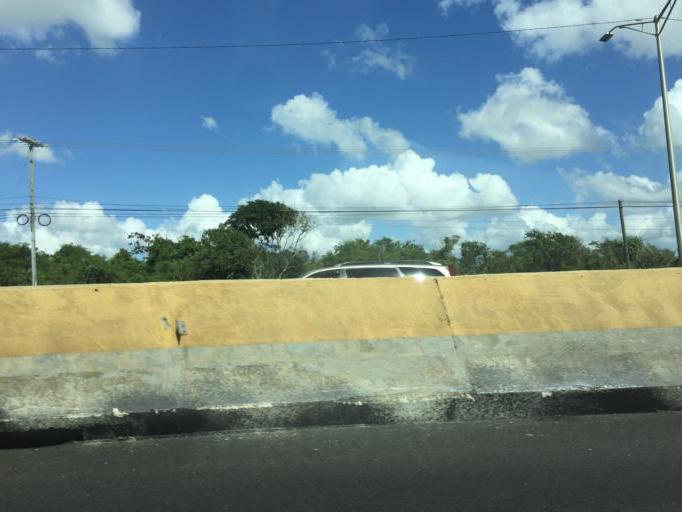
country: DO
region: Santo Domingo
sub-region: Santo Domingo
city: Santo Domingo Este
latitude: 18.4643
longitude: -69.7600
